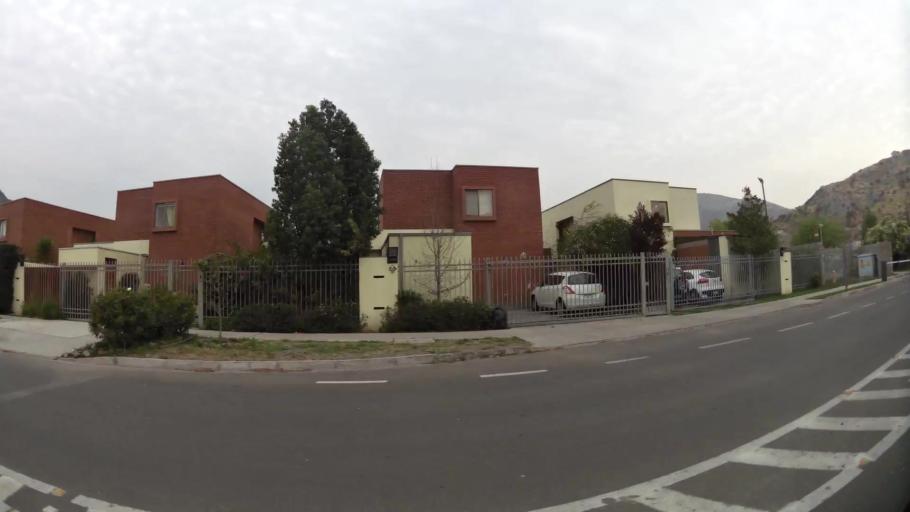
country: CL
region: Santiago Metropolitan
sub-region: Provincia de Chacabuco
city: Chicureo Abajo
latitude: -33.3112
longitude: -70.6573
